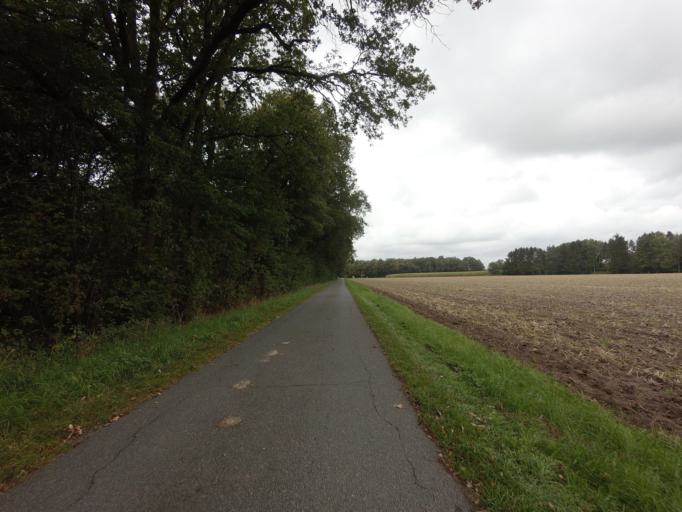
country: DE
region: North Rhine-Westphalia
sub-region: Regierungsbezirk Munster
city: Gronau
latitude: 52.2541
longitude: 7.0770
